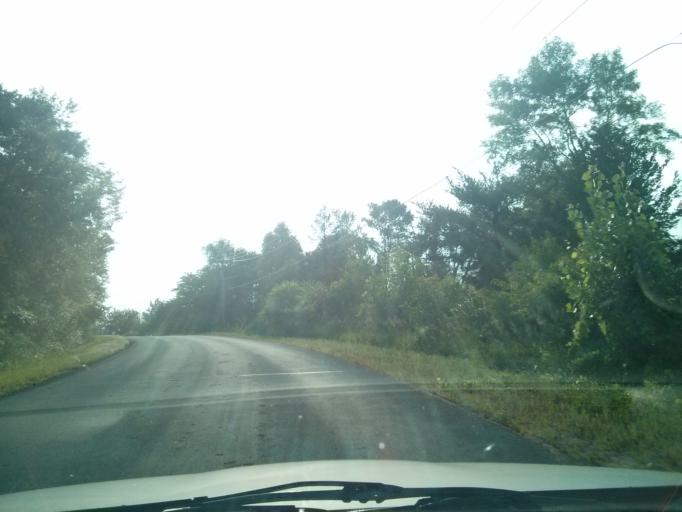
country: US
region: Wisconsin
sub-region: Saint Croix County
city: Hudson
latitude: 44.9795
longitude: -92.7113
